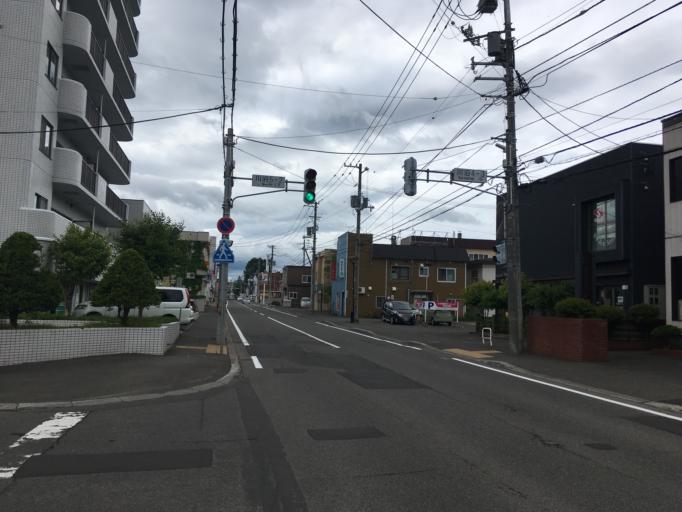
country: JP
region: Hokkaido
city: Sapporo
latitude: 42.9944
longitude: 141.3317
